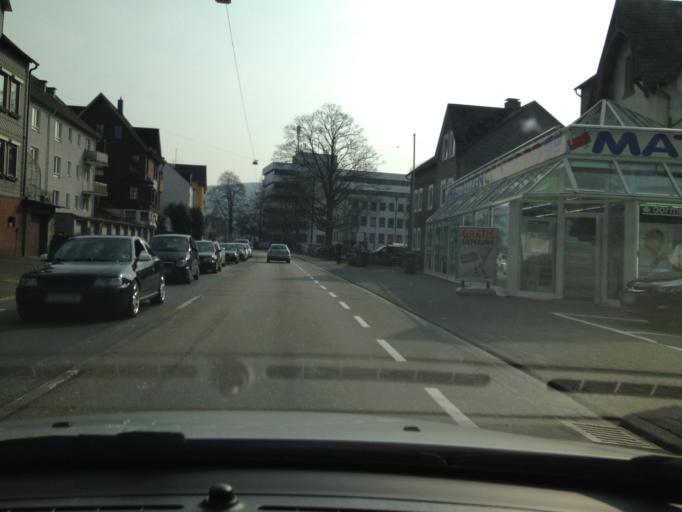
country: DE
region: North Rhine-Westphalia
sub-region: Regierungsbezirk Arnsberg
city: Siegen
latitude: 50.8457
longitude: 7.9872
